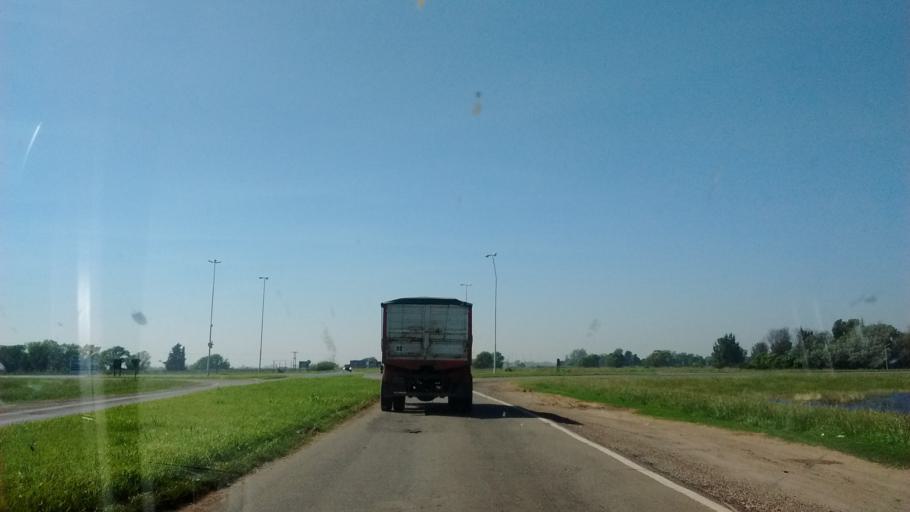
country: AR
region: Buenos Aires
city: General Villegas
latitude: -35.0348
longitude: -62.9885
